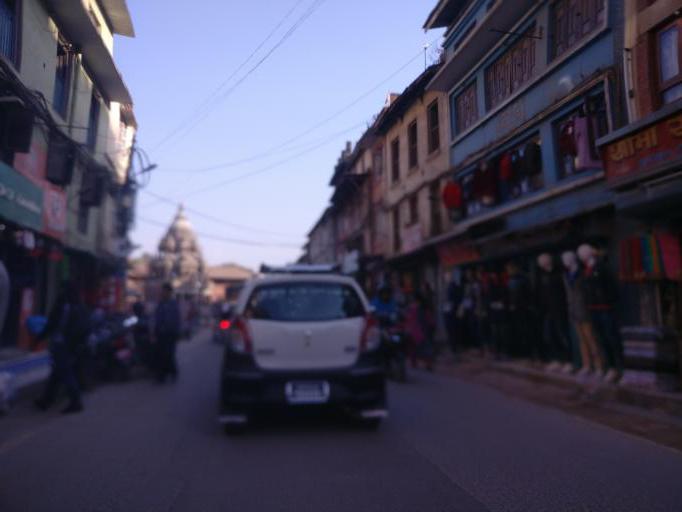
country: NP
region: Central Region
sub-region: Bagmati Zone
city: Patan
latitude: 27.6732
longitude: 85.3242
